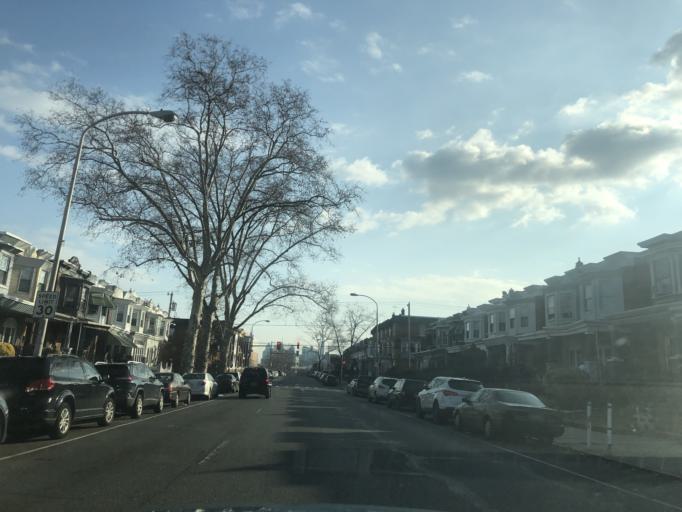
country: US
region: Pennsylvania
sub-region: Delaware County
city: Millbourne
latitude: 39.9581
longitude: -75.2223
